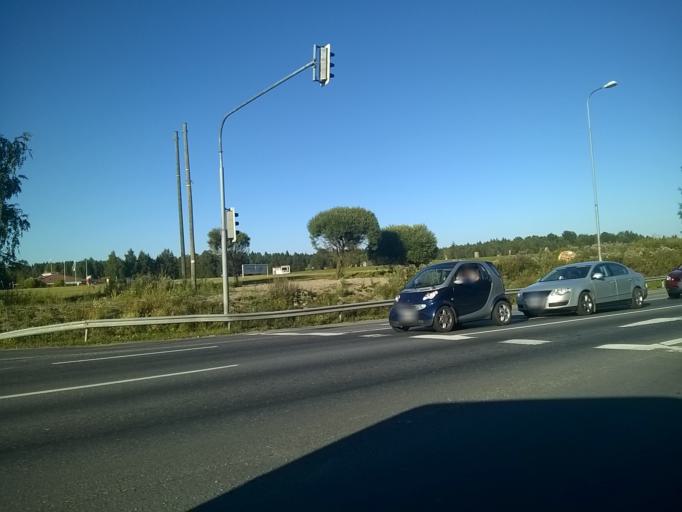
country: FI
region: Pirkanmaa
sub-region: Tampere
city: Tampere
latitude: 61.5054
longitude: 23.8458
